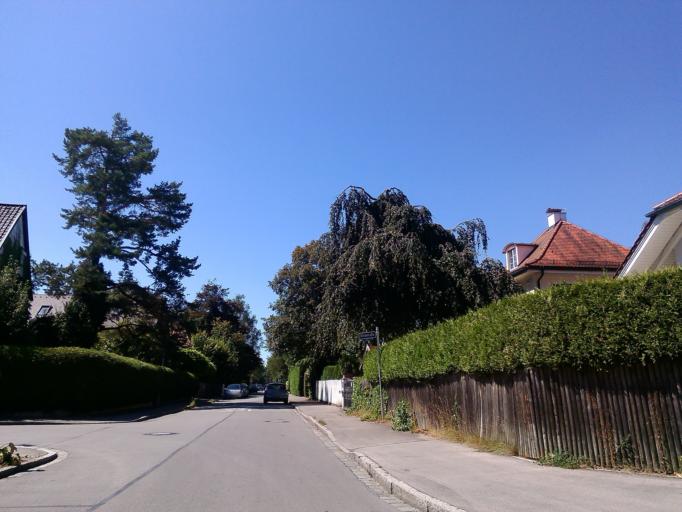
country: DE
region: Bavaria
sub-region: Upper Bavaria
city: Grafelfing
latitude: 48.1209
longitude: 11.4207
